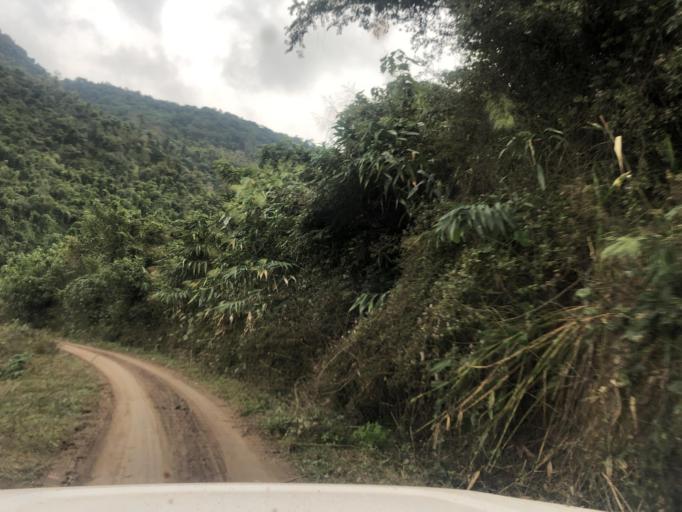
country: LA
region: Phongsali
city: Khoa
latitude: 21.2941
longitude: 102.5859
